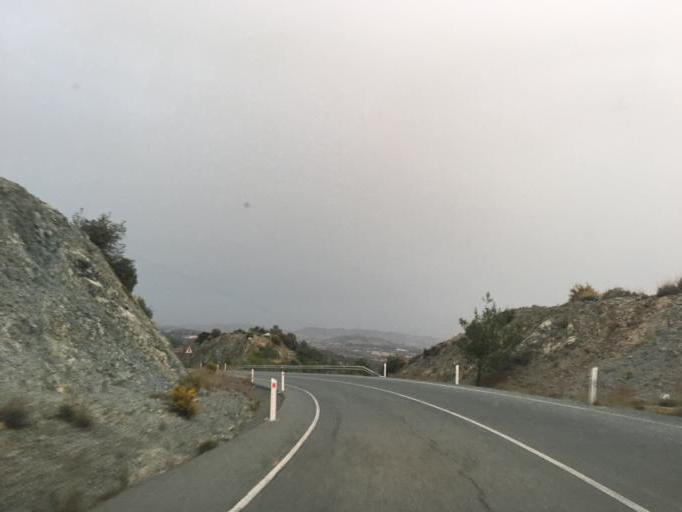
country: CY
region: Limassol
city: Parekklisha
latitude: 34.7883
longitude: 33.1604
